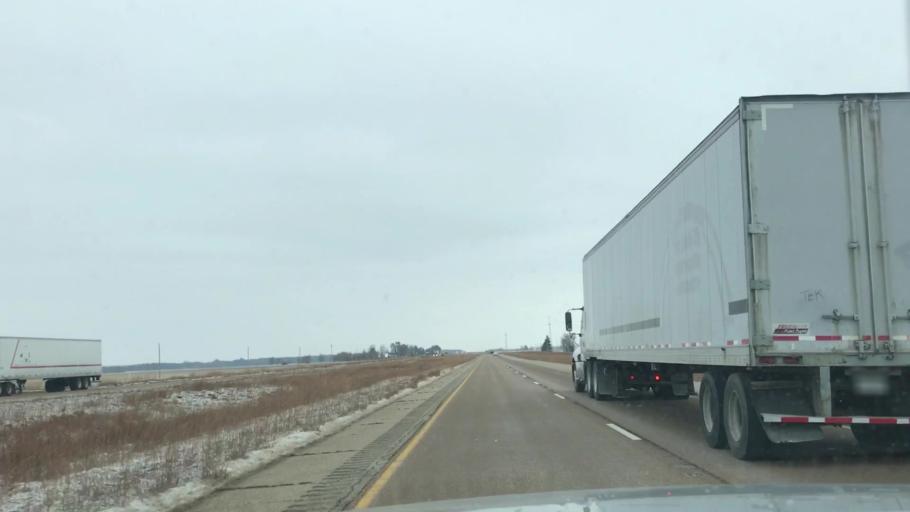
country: US
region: Illinois
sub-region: Montgomery County
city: Raymond
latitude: 39.4031
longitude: -89.6431
